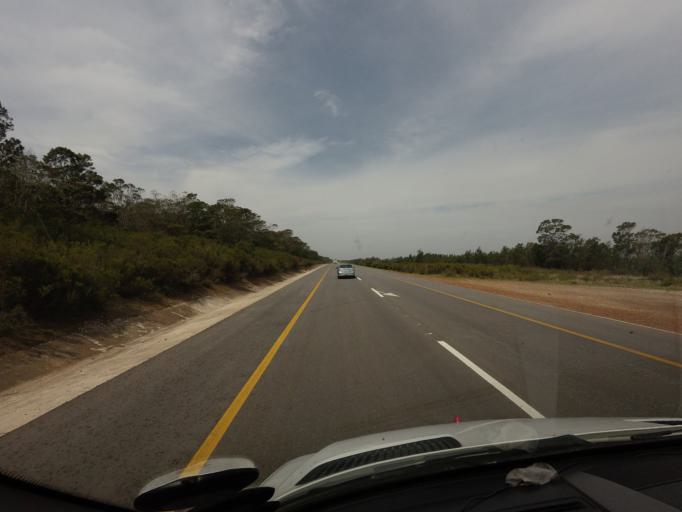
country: ZA
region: Eastern Cape
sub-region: Cacadu District Municipality
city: Kruisfontein
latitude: -33.9955
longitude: 24.7134
